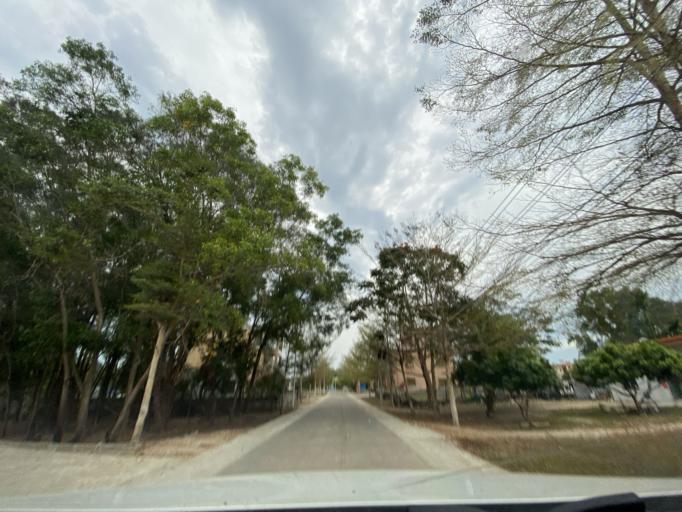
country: CN
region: Hainan
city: Yingzhou
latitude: 18.4210
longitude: 109.8219
